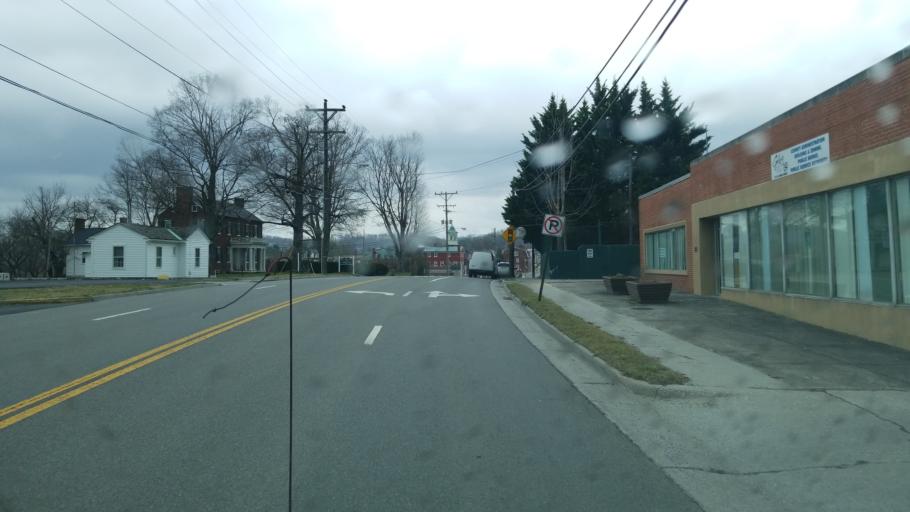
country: US
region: Virginia
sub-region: Giles County
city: Pearisburg
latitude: 37.3290
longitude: -80.7367
